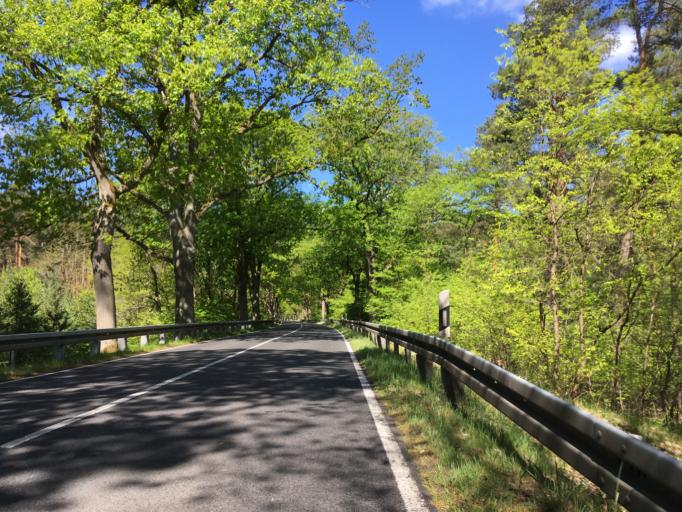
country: DE
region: Brandenburg
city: Birkenwerder
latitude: 52.7184
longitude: 13.3399
